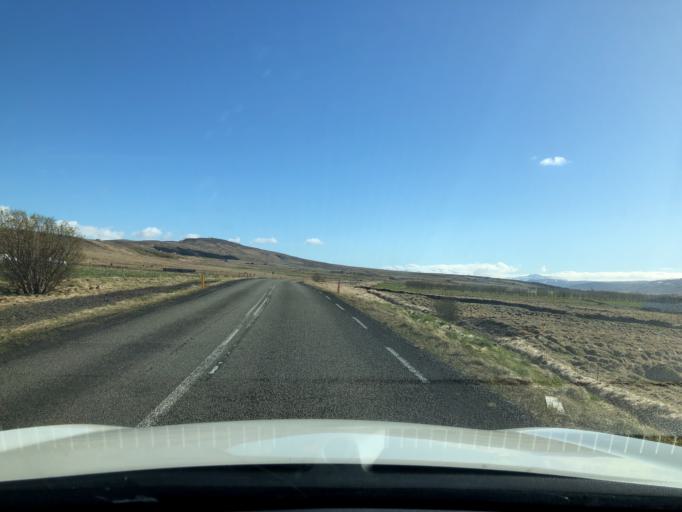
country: IS
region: West
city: Borgarnes
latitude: 64.6646
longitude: -21.3706
